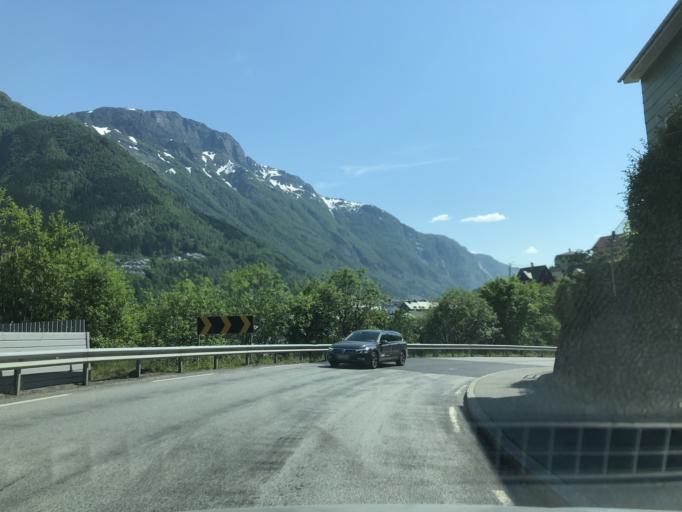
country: NO
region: Hordaland
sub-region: Odda
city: Odda
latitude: 60.0724
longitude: 6.5393
